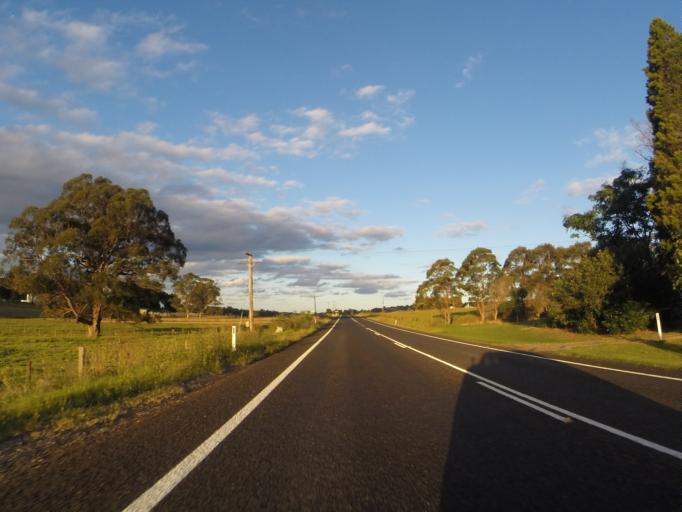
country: AU
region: New South Wales
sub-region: Shellharbour
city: Calderwood
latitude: -34.5774
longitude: 150.7360
